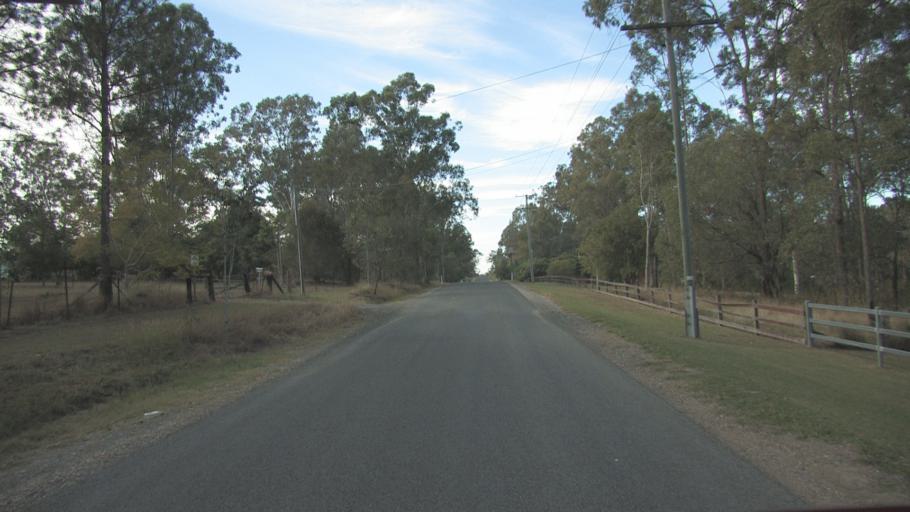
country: AU
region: Queensland
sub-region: Logan
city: North Maclean
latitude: -27.7731
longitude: 152.9741
